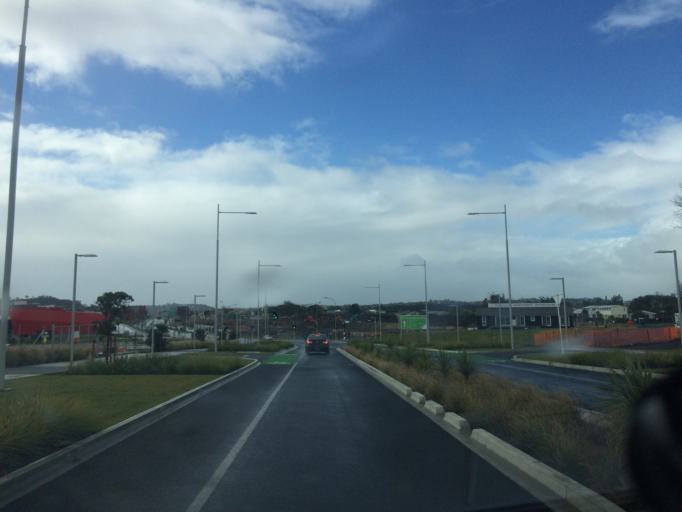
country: NZ
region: Auckland
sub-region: Auckland
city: Rosebank
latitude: -36.7966
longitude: 174.6515
